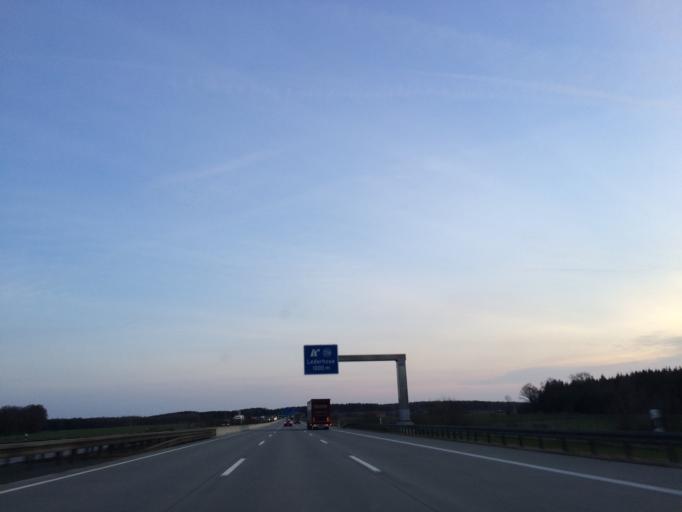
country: DE
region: Thuringia
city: Schwarzbach
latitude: 50.7930
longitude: 11.8953
